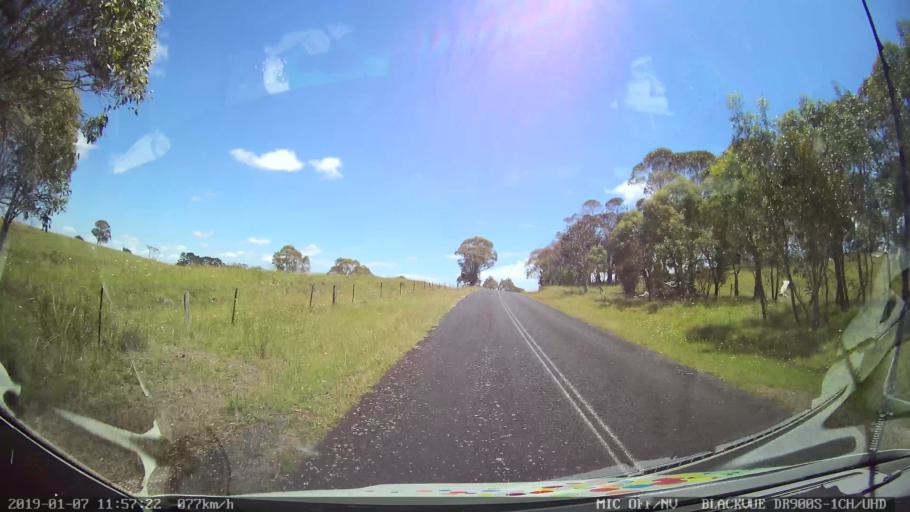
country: AU
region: New South Wales
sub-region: Guyra
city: Guyra
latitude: -30.2653
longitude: 151.6661
